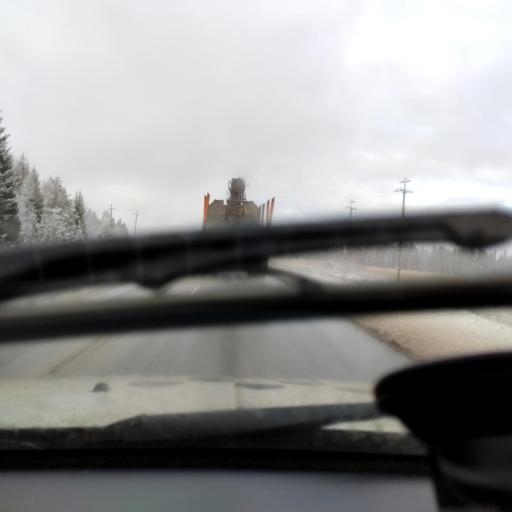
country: RU
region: Perm
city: Nytva
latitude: 57.9624
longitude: 55.3627
